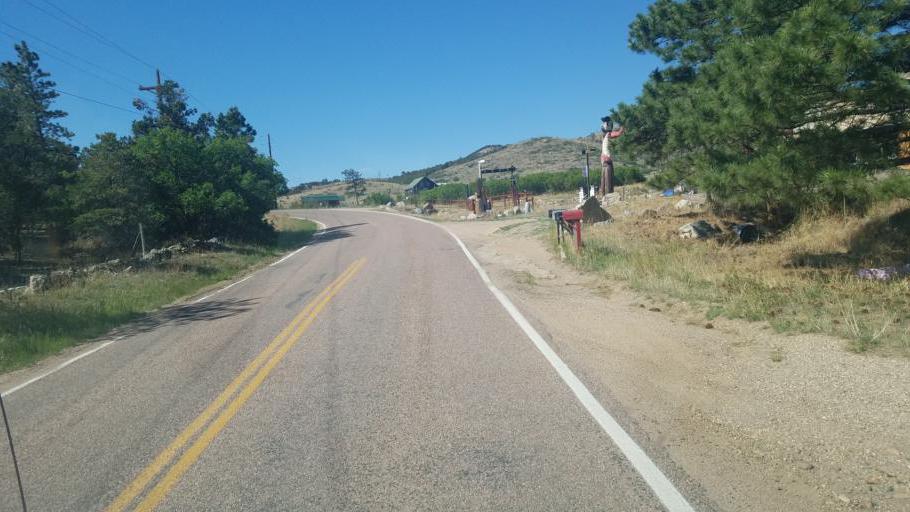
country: US
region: Colorado
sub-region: Custer County
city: Westcliffe
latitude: 38.3369
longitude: -105.4857
